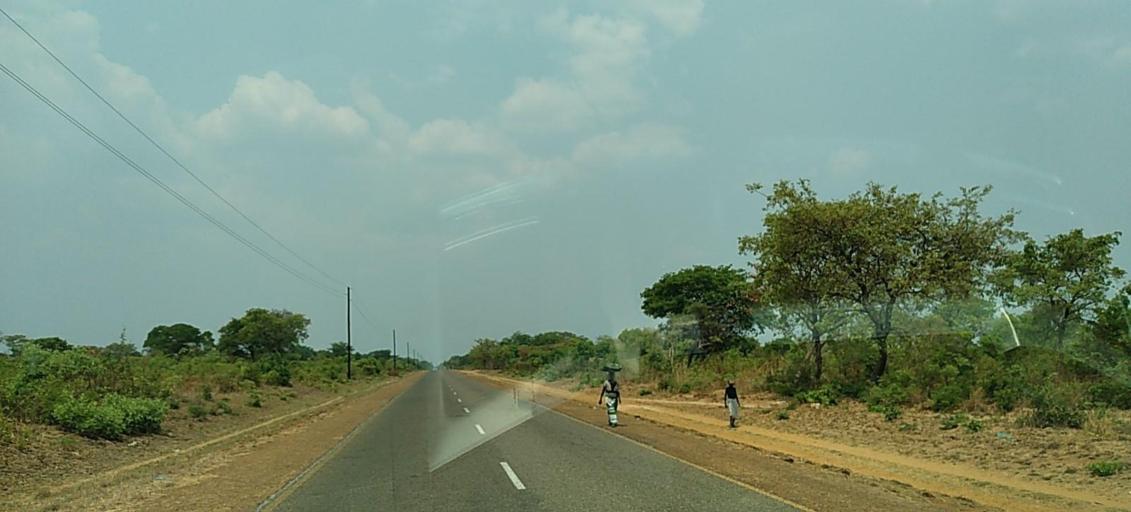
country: ZM
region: North-Western
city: Zambezi
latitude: -13.5522
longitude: 23.1360
